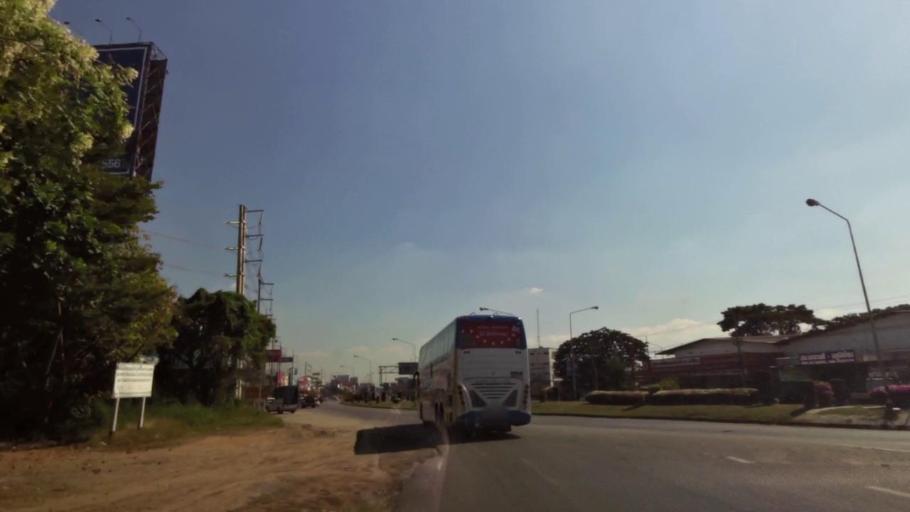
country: TH
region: Nakhon Sawan
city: Nakhon Sawan
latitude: 15.7059
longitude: 100.1120
